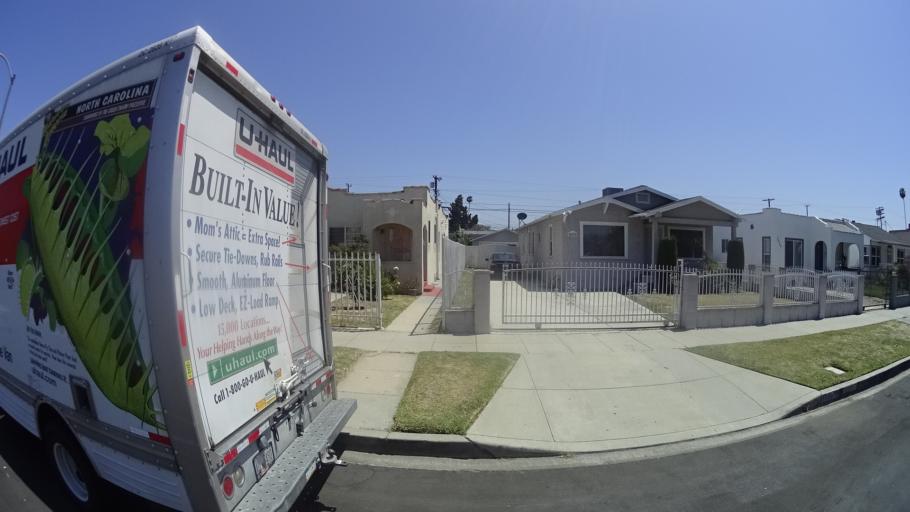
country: US
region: California
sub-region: Los Angeles County
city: View Park-Windsor Hills
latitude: 33.9940
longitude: -118.3032
